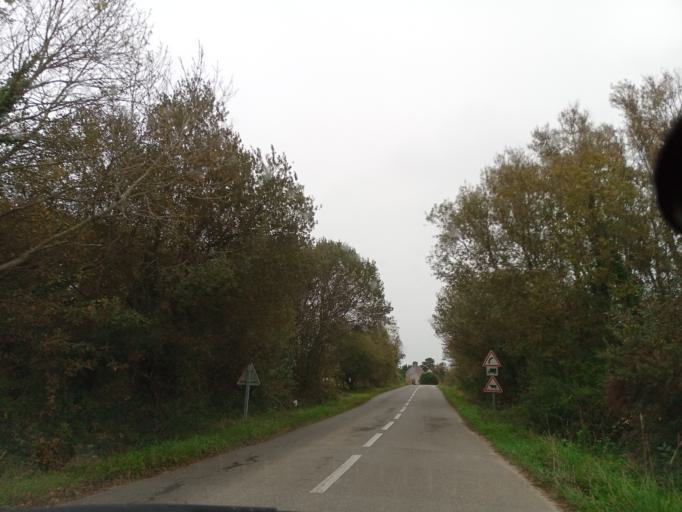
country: FR
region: Brittany
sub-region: Departement du Finistere
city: Esquibien
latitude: 48.0186
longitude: -4.5612
